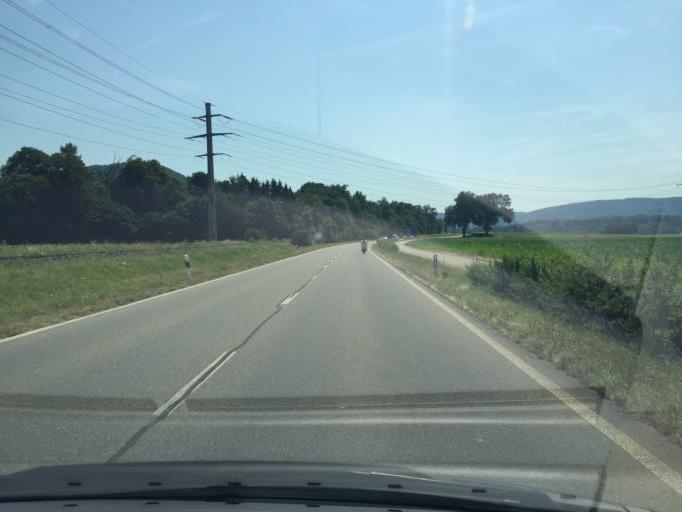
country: CH
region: Schaffhausen
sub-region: Bezirk Stein
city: Ramsen
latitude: 47.6903
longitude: 8.8271
